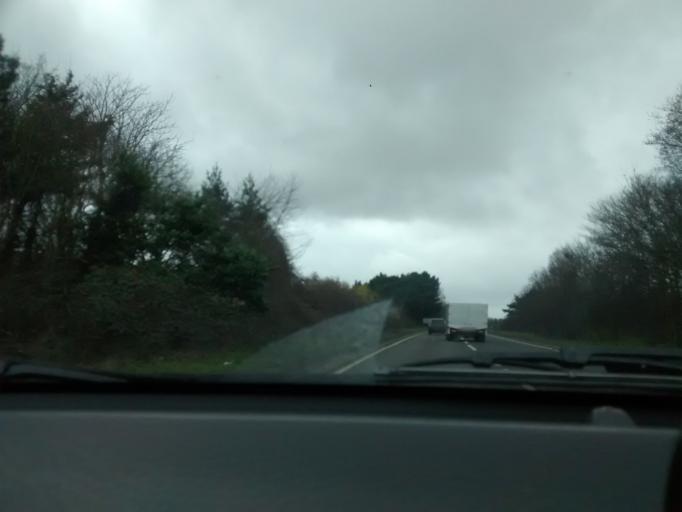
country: GB
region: England
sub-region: Suffolk
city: Felixstowe
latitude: 51.9797
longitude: 1.3290
